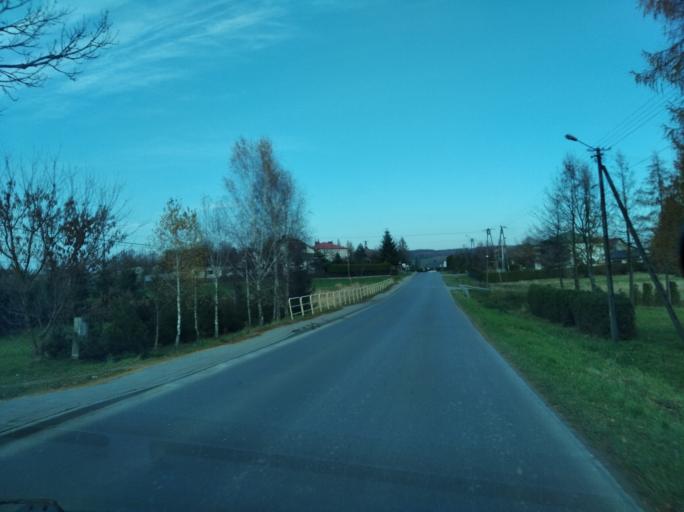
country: PL
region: Subcarpathian Voivodeship
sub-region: Powiat ropczycko-sedziszowski
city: Iwierzyce
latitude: 50.0243
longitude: 21.7553
